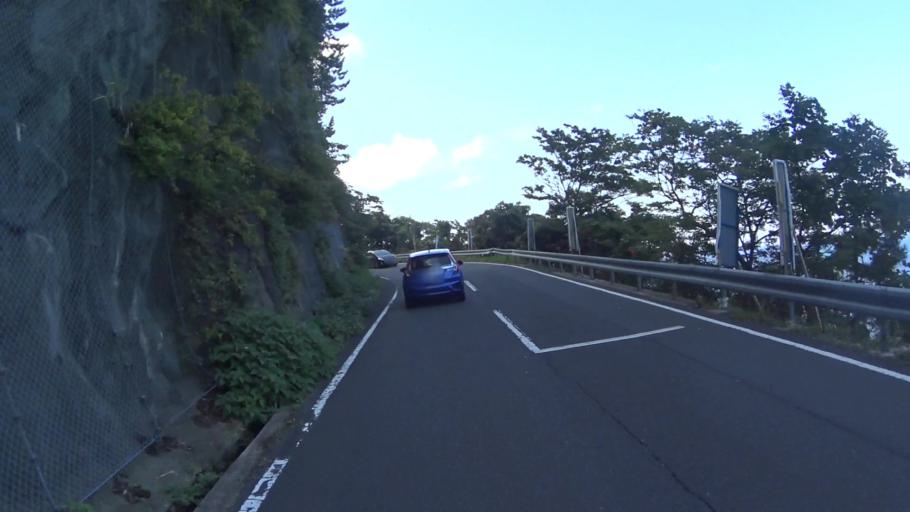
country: JP
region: Kyoto
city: Miyazu
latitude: 35.7564
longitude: 135.2499
